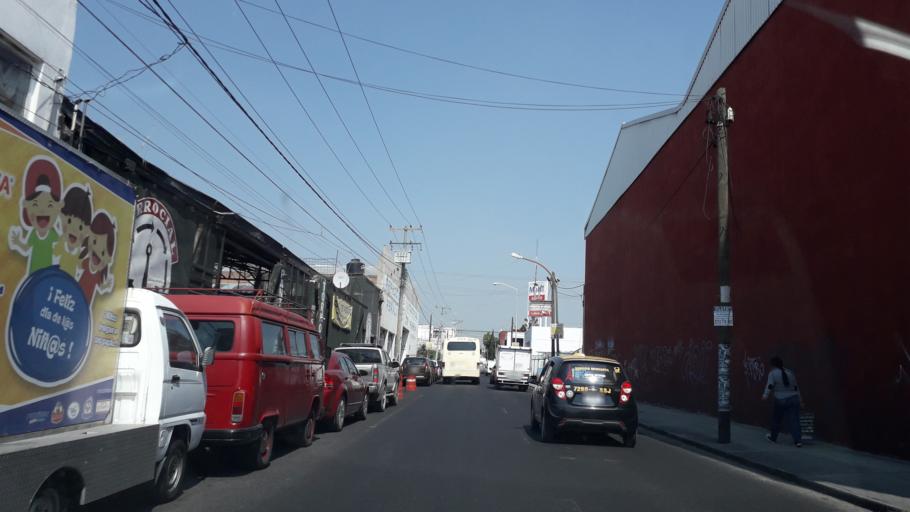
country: MX
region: Puebla
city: Puebla
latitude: 19.0518
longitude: -98.2108
